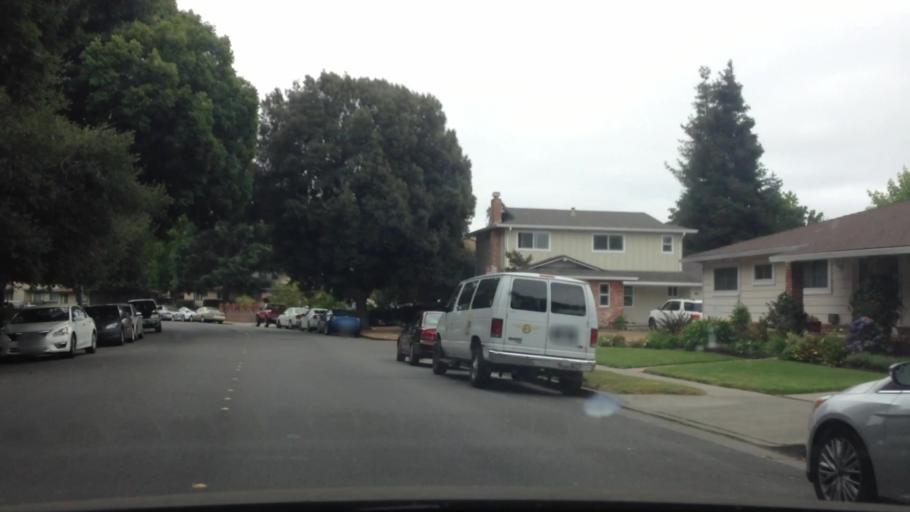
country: US
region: California
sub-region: Alameda County
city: Fremont
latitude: 37.5587
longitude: -121.9960
